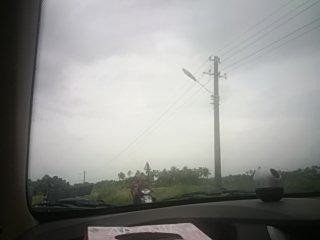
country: IN
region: Goa
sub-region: South Goa
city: Cavelossim
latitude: 15.1813
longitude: 73.9550
